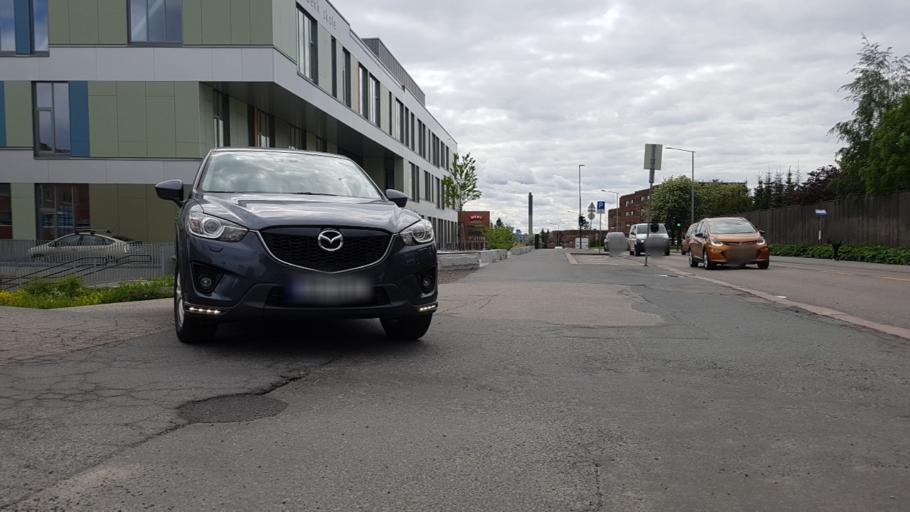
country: NO
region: Oslo
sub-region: Oslo
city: Oslo
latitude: 59.9378
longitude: 10.8256
